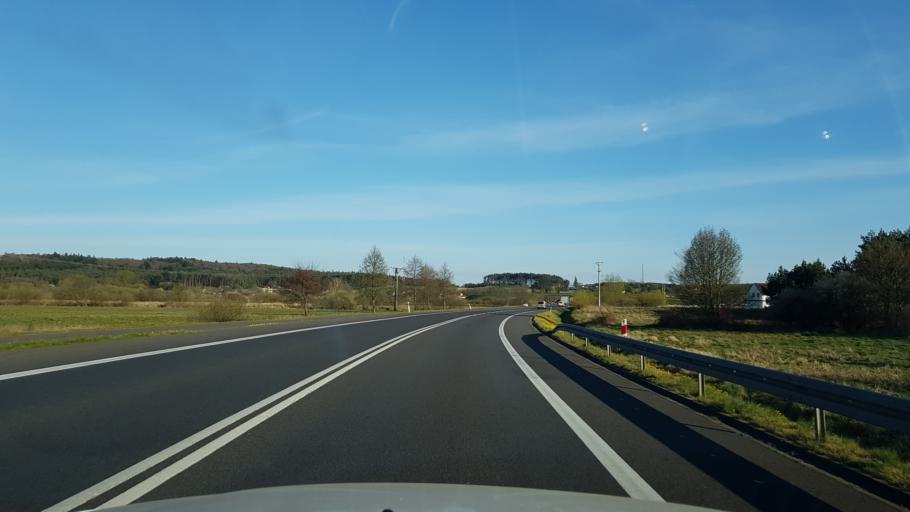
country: PL
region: West Pomeranian Voivodeship
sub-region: Powiat kamienski
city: Wolin
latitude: 53.8784
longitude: 14.5335
